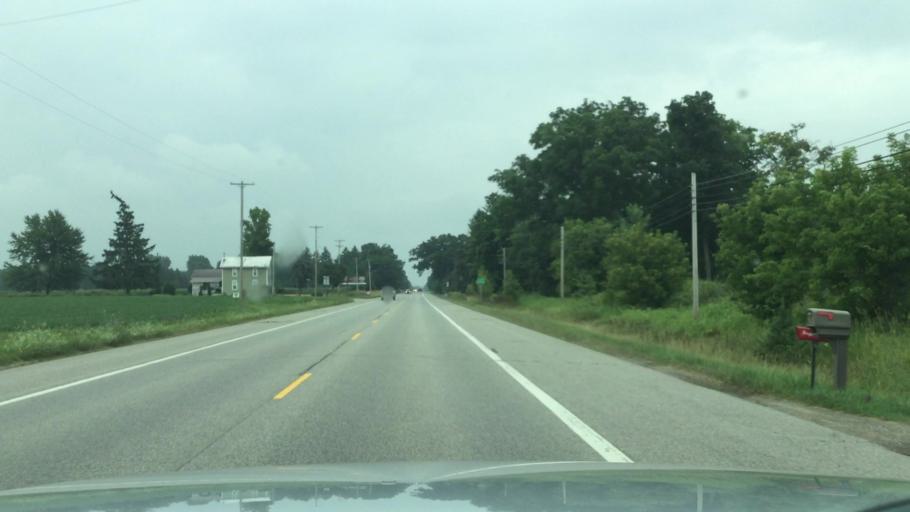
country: US
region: Michigan
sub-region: Shiawassee County
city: Owosso
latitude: 43.0438
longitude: -84.1770
